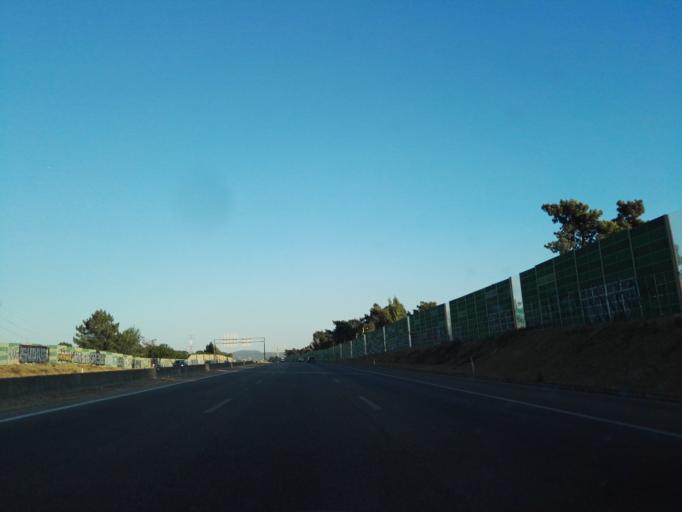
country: PT
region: Setubal
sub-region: Seixal
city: Arrentela
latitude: 38.6027
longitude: -9.0948
